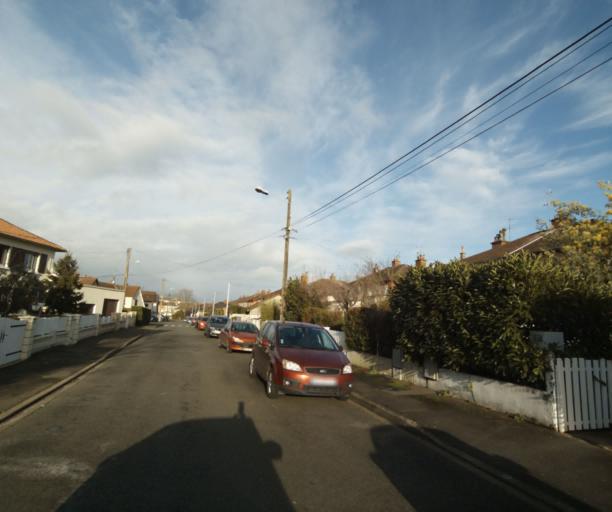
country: FR
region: Pays de la Loire
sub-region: Departement de la Sarthe
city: Le Mans
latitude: 47.9625
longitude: 0.2042
